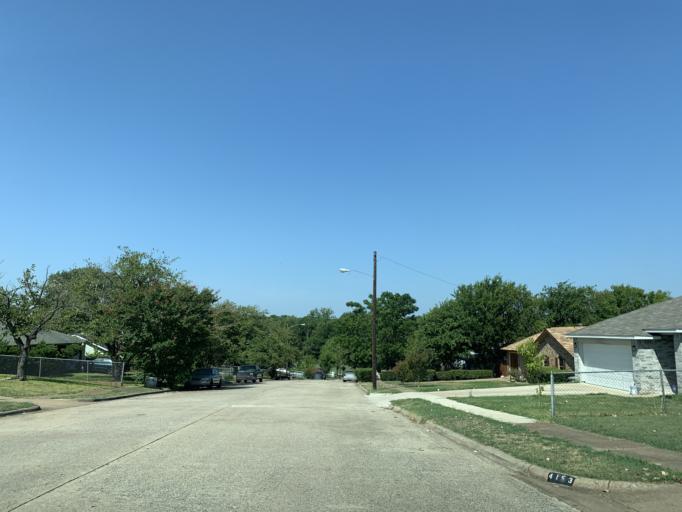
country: US
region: Texas
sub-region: Dallas County
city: Hutchins
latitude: 32.6676
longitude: -96.7472
